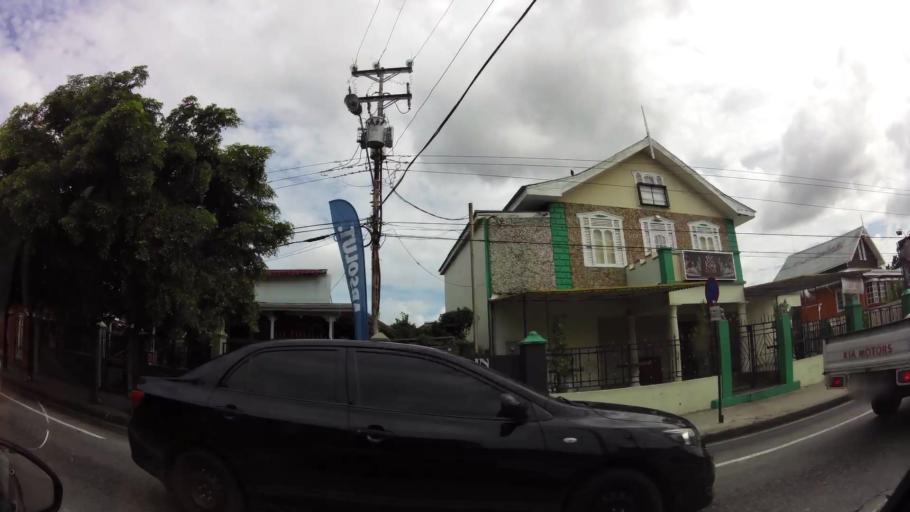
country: TT
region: City of Port of Spain
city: Port-of-Spain
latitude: 10.6606
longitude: -61.5216
